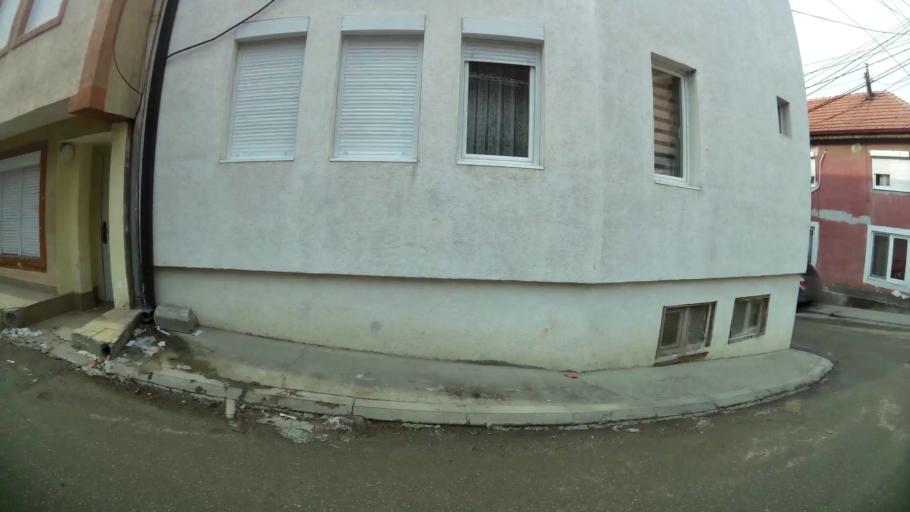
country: MK
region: Cair
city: Cair
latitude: 42.0048
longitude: 21.4472
